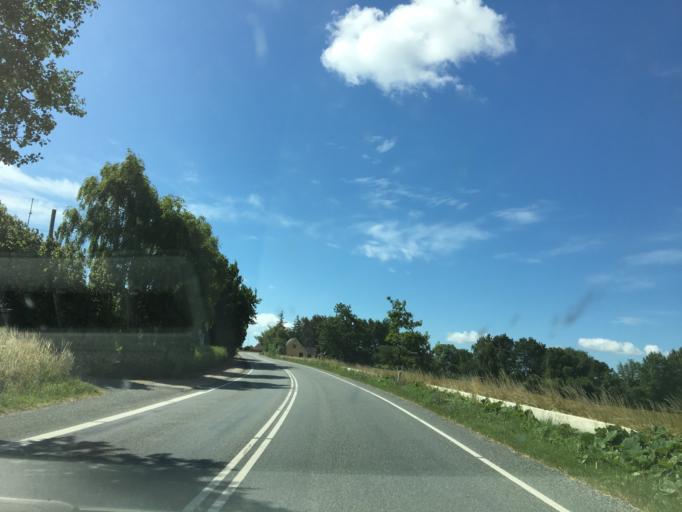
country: DK
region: South Denmark
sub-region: Langeland Kommune
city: Rudkobing
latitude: 54.9212
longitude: 10.7332
